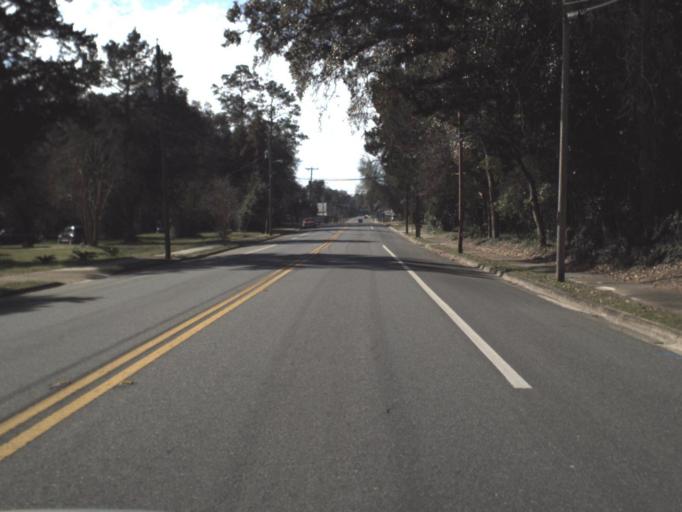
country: US
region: Florida
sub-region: Jackson County
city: Malone
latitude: 30.8736
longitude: -85.1620
